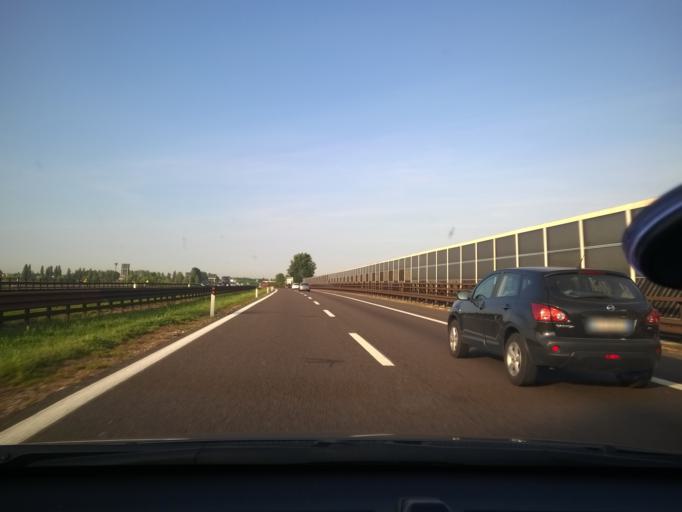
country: IT
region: Veneto
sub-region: Provincia di Verona
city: Nogarole Rocca
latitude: 45.2890
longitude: 10.8882
